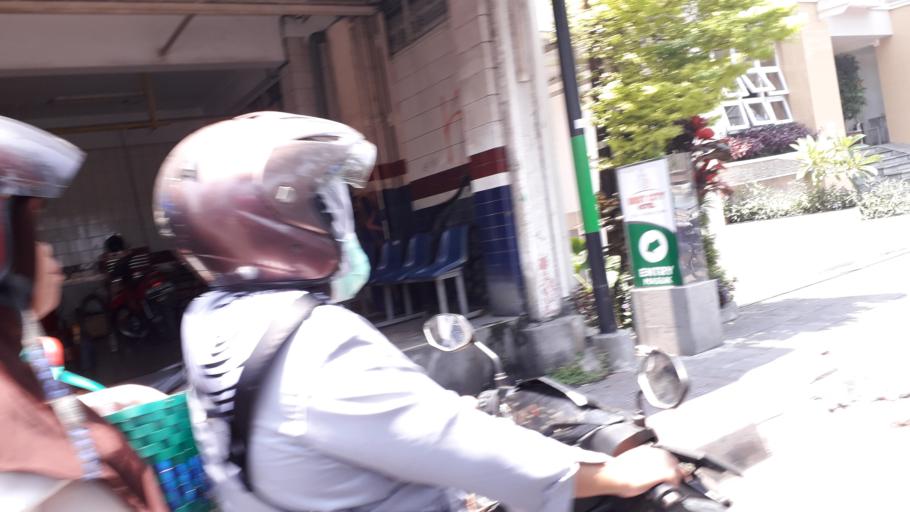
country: ID
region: Daerah Istimewa Yogyakarta
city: Yogyakarta
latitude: -7.7832
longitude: 110.3608
